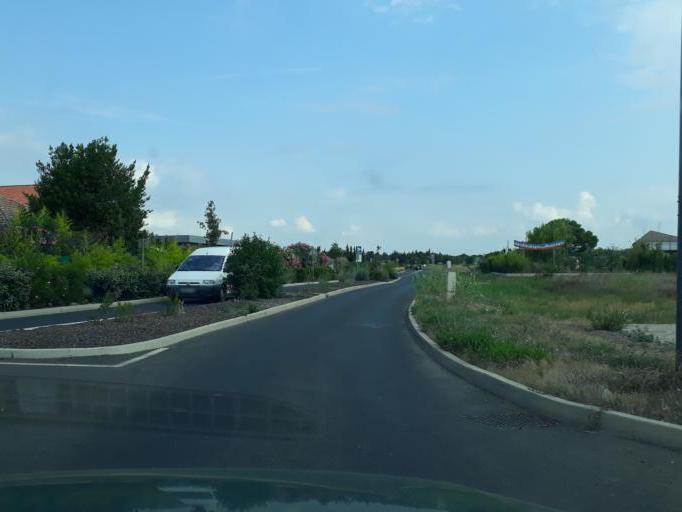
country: FR
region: Languedoc-Roussillon
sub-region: Departement de l'Herault
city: Agde
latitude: 43.2883
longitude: 3.4816
